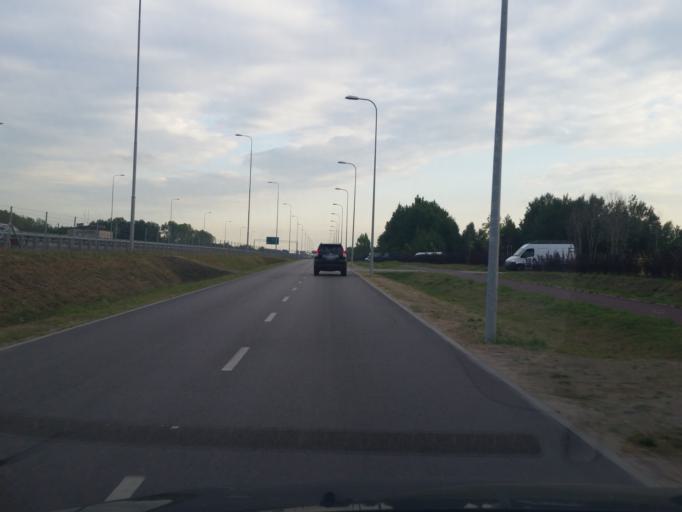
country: PL
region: Masovian Voivodeship
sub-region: Warszawa
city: Wlochy
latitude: 52.1543
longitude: 20.9871
